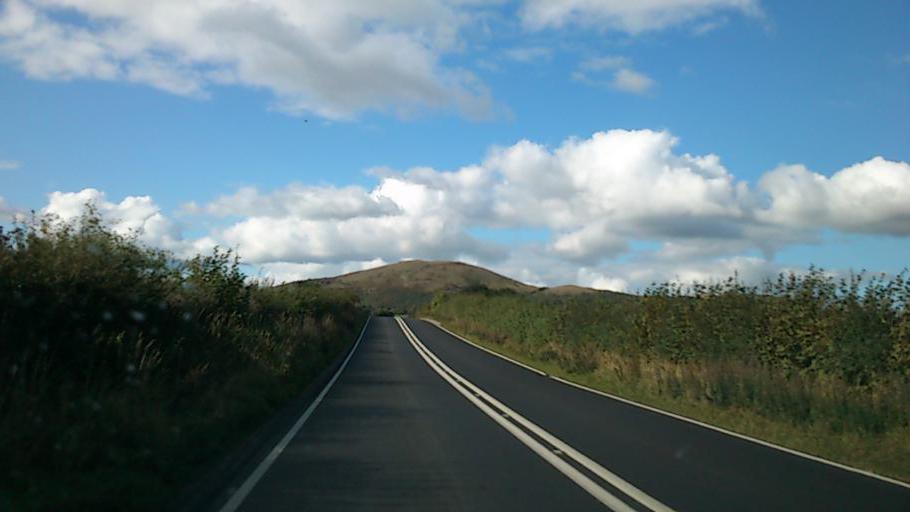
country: GB
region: England
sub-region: Shropshire
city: Westbury
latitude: 52.7034
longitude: -3.0010
